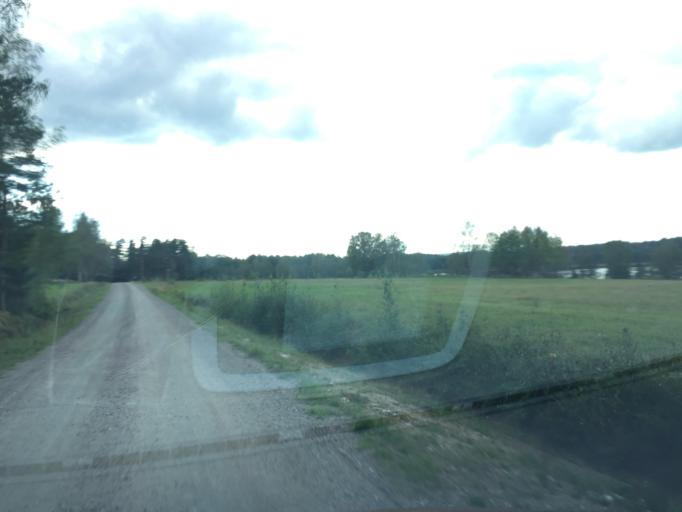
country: SE
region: Soedermanland
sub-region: Vingakers Kommun
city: Vingaker
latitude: 58.9923
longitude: 15.7377
